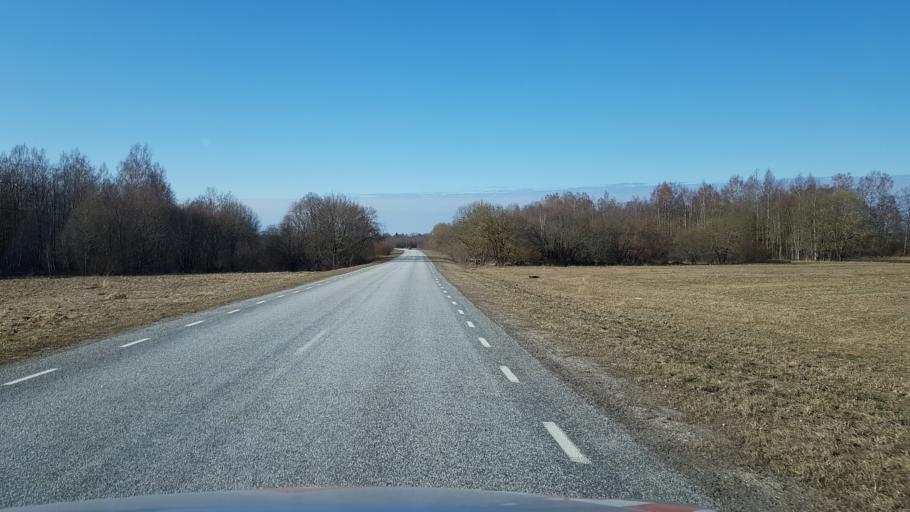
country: EE
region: Laeaene-Virumaa
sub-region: Haljala vald
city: Haljala
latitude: 59.4807
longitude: 26.1553
